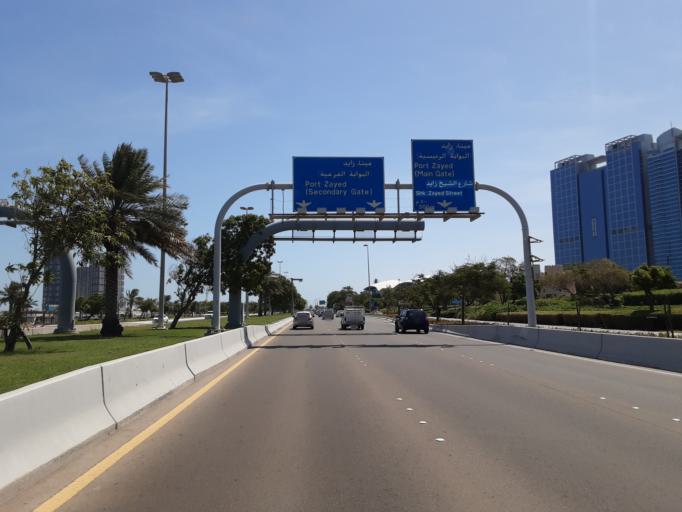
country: AE
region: Abu Dhabi
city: Abu Dhabi
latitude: 24.5065
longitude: 54.3713
